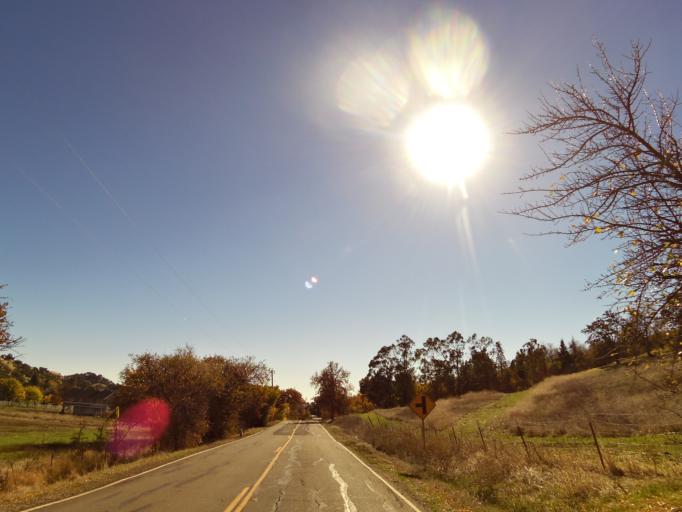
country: US
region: California
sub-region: Solano County
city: Vacaville
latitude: 38.4257
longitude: -122.0471
